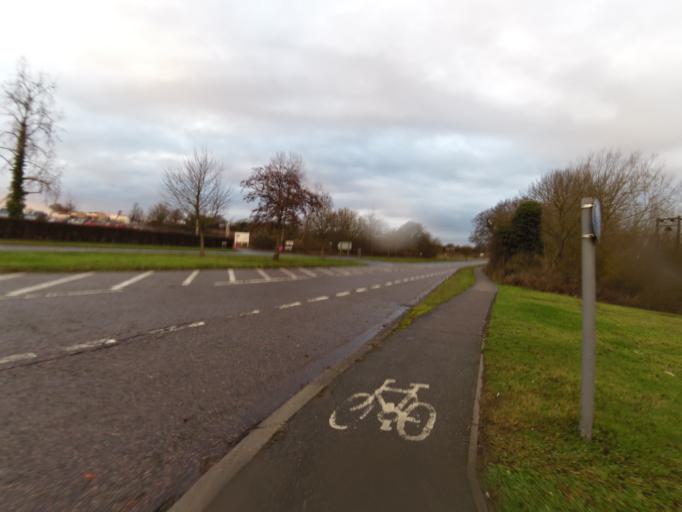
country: GB
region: England
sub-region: Suffolk
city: Stowmarket
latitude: 52.1729
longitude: 1.0161
